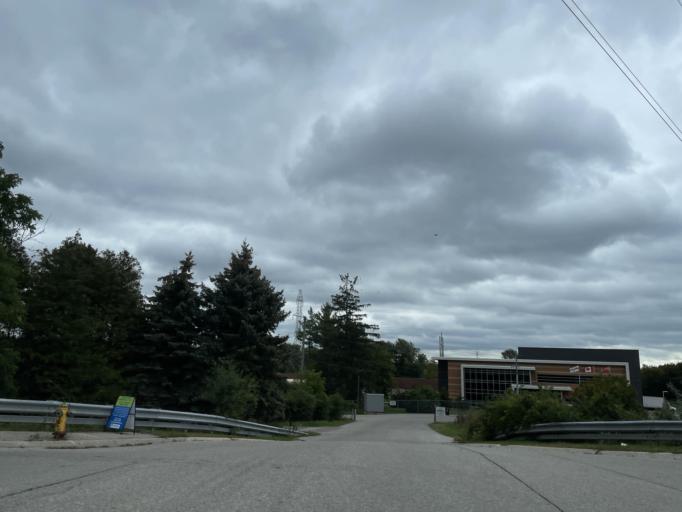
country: CA
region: Ontario
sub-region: Wellington County
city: Guelph
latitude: 43.5231
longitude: -80.2672
